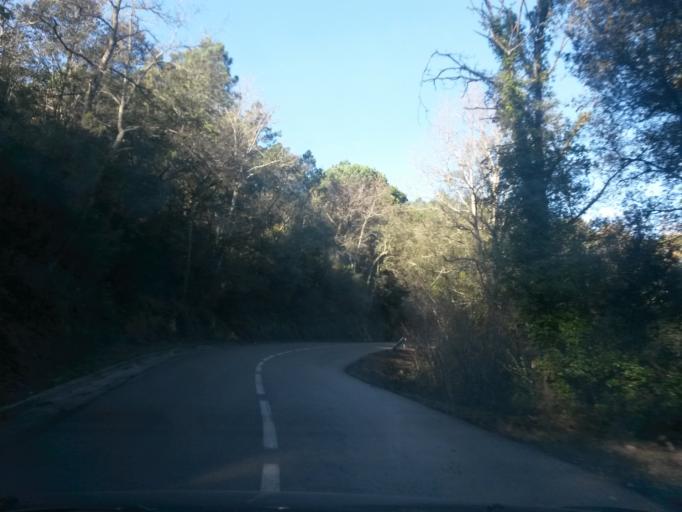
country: ES
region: Catalonia
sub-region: Provincia de Girona
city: Angles
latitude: 41.9974
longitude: 2.6690
